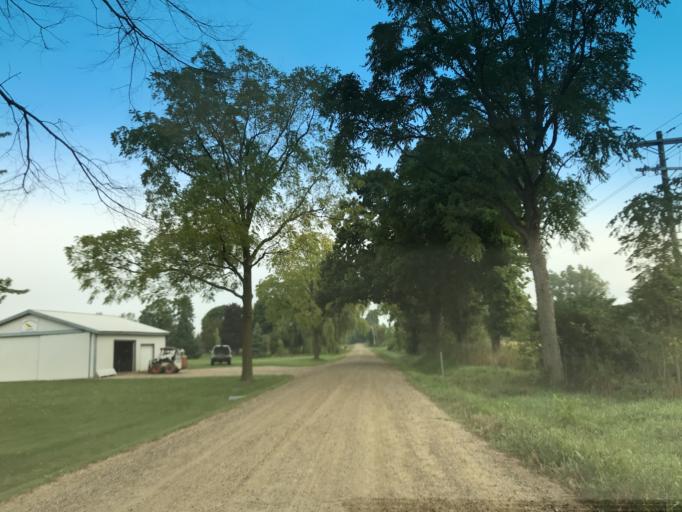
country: US
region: Michigan
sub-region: Eaton County
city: Grand Ledge
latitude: 42.8060
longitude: -84.7788
